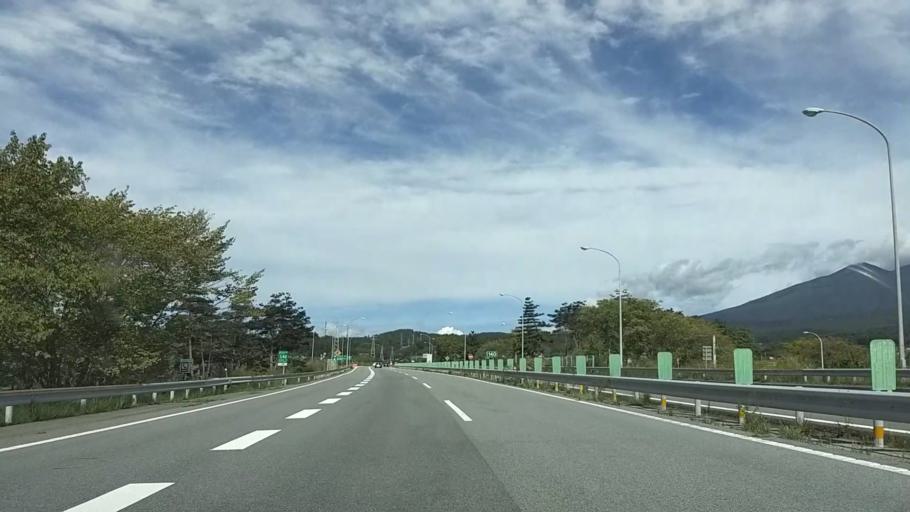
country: JP
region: Yamanashi
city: Nirasaki
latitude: 35.8354
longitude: 138.3898
